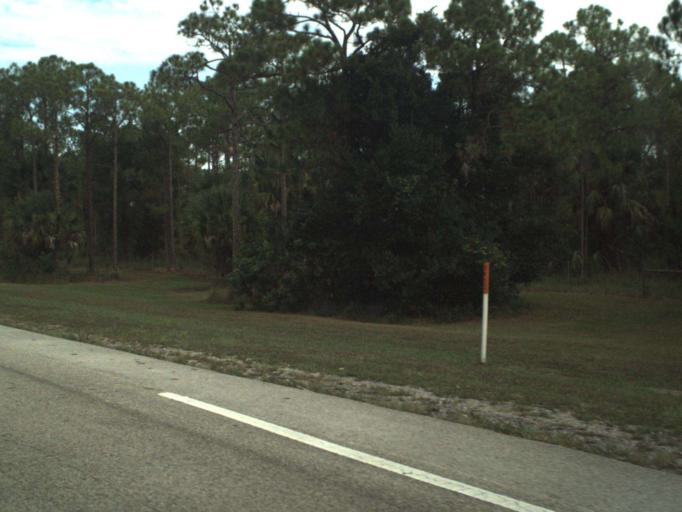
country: US
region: Florida
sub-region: Martin County
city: Palm City
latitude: 27.1276
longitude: -80.3385
